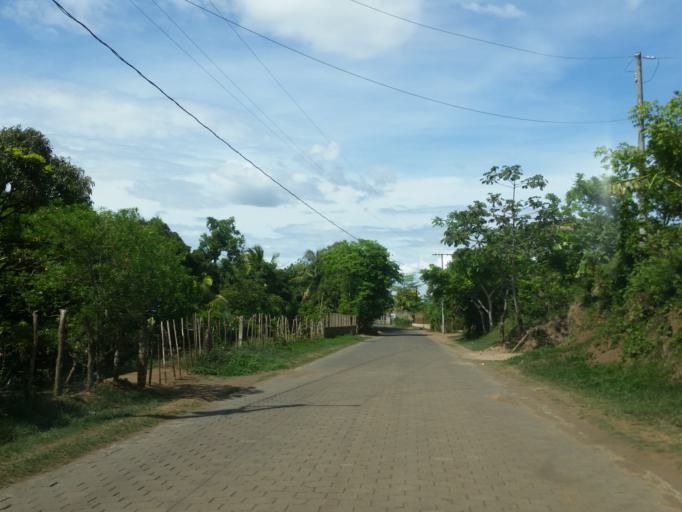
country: NI
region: Masaya
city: Masaya
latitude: 11.9702
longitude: -86.0287
